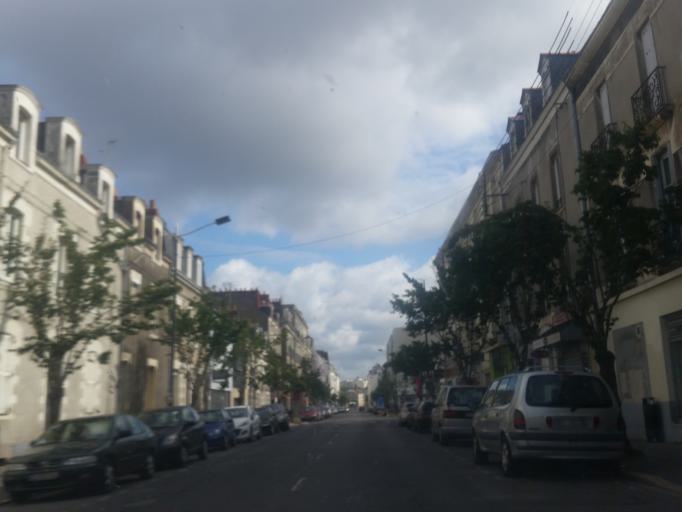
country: FR
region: Pays de la Loire
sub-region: Departement de la Loire-Atlantique
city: Nantes
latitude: 47.2226
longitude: -1.5306
